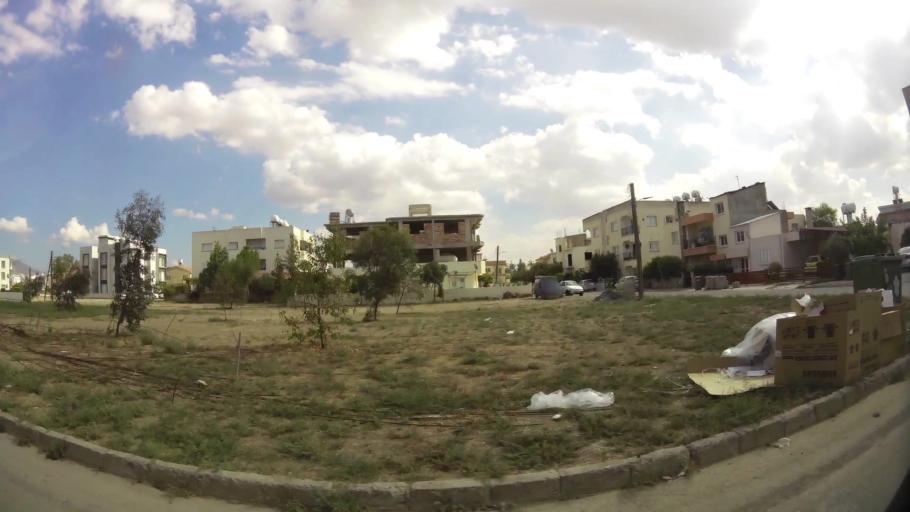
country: CY
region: Lefkosia
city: Nicosia
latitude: 35.2166
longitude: 33.2992
